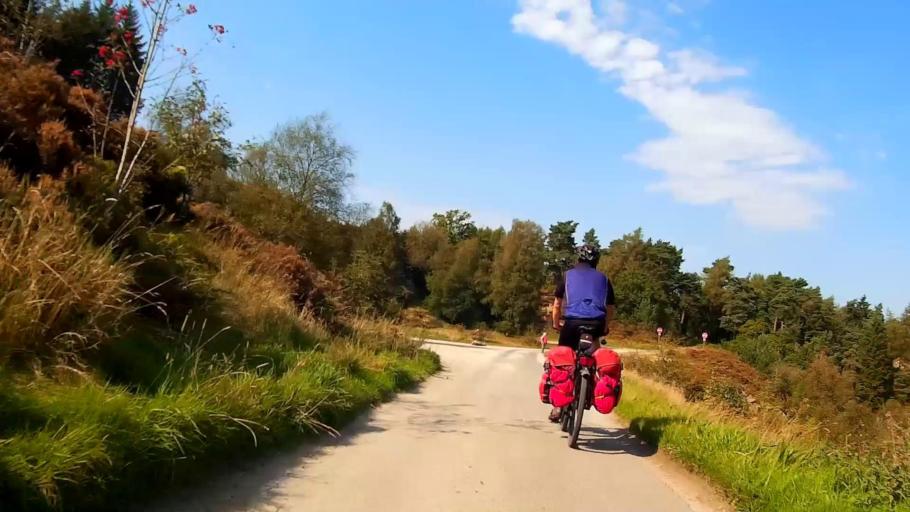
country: GB
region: England
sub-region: Derbyshire
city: Whaley Bridge
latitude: 53.2572
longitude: -1.9835
